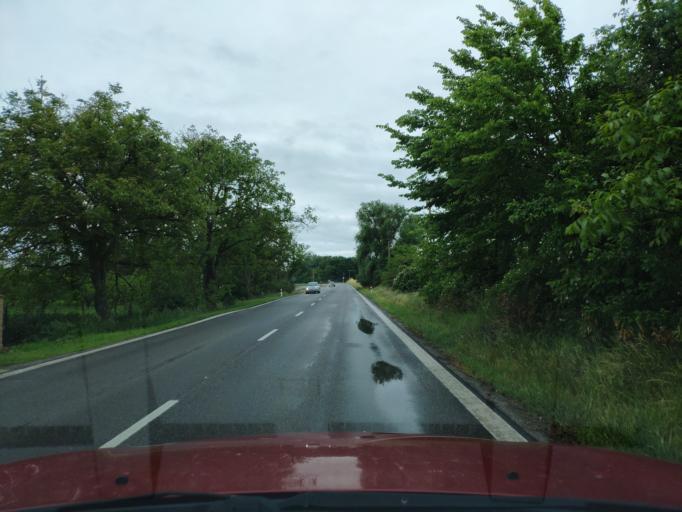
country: HU
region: Borsod-Abauj-Zemplen
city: Karcsa
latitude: 48.3955
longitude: 21.8036
